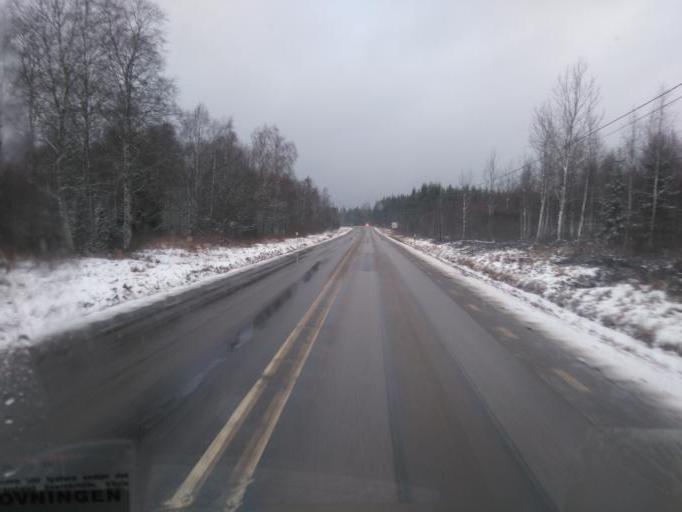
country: SE
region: Joenkoeping
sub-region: Eksjo Kommun
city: Mariannelund
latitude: 57.6342
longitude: 15.6308
